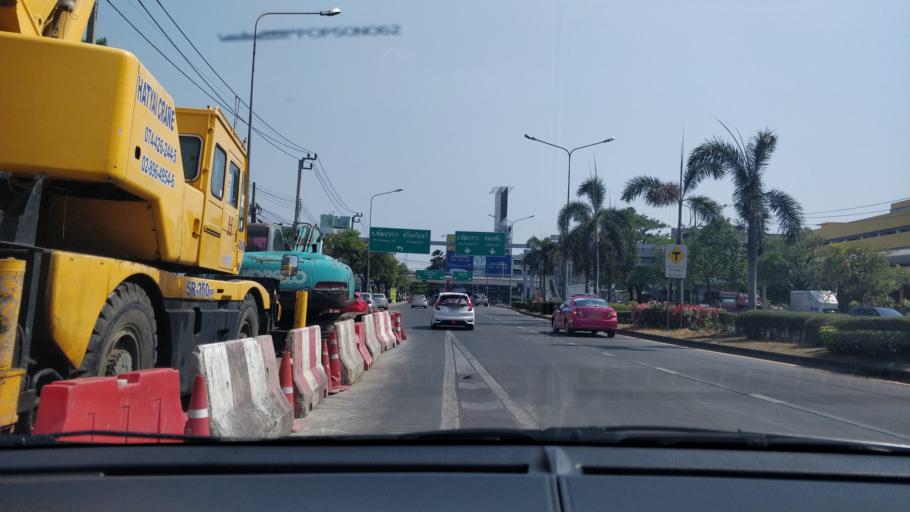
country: TH
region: Bangkok
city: Watthana
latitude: 13.7383
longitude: 100.6164
